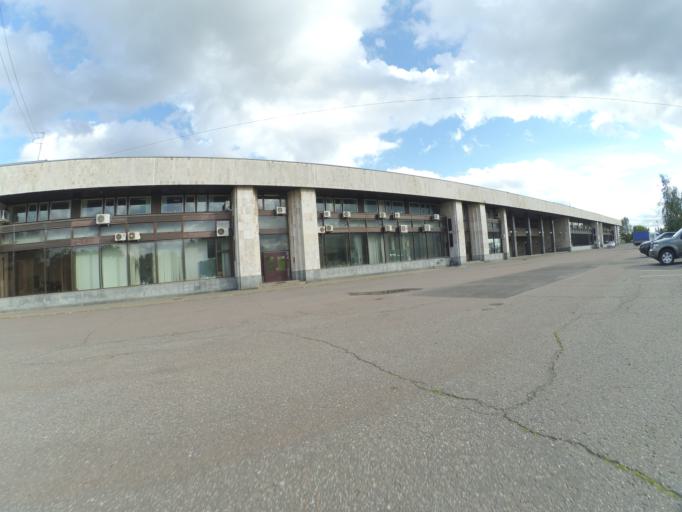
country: RU
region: Moskovskaya
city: Kastanayevo
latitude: 55.7300
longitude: 37.5113
